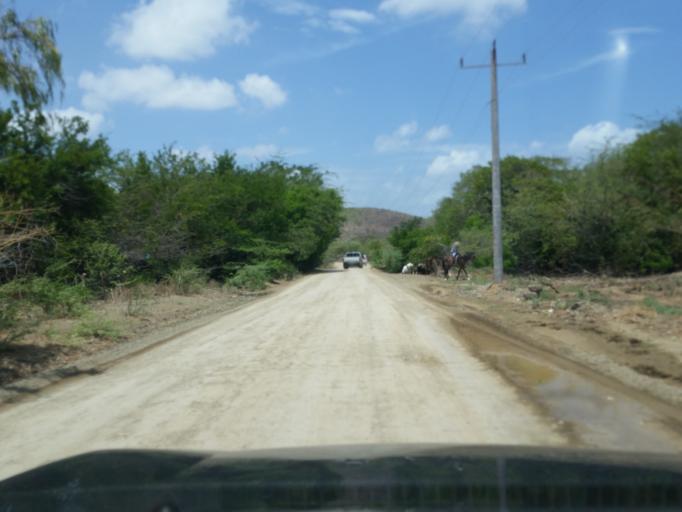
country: NI
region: Rivas
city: Tola
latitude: 11.4684
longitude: -86.1004
